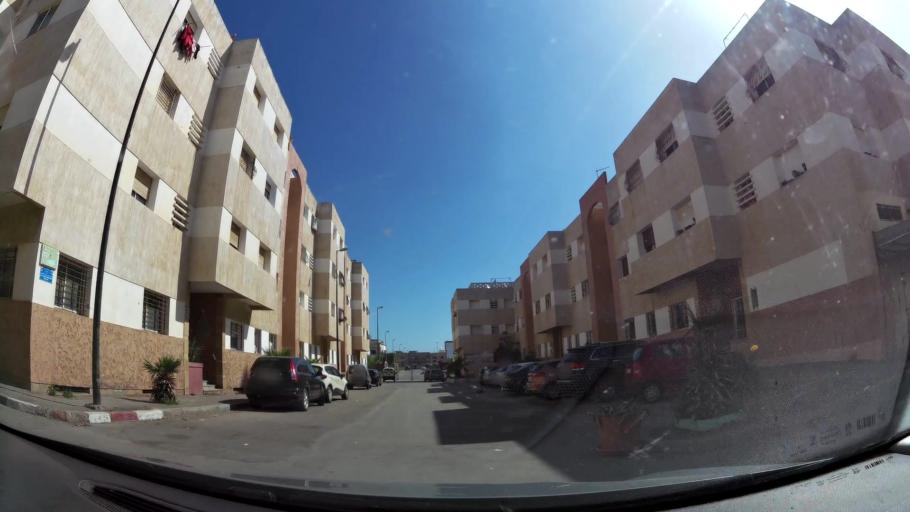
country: MA
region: Rabat-Sale-Zemmour-Zaer
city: Sale
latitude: 34.0648
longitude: -6.8065
